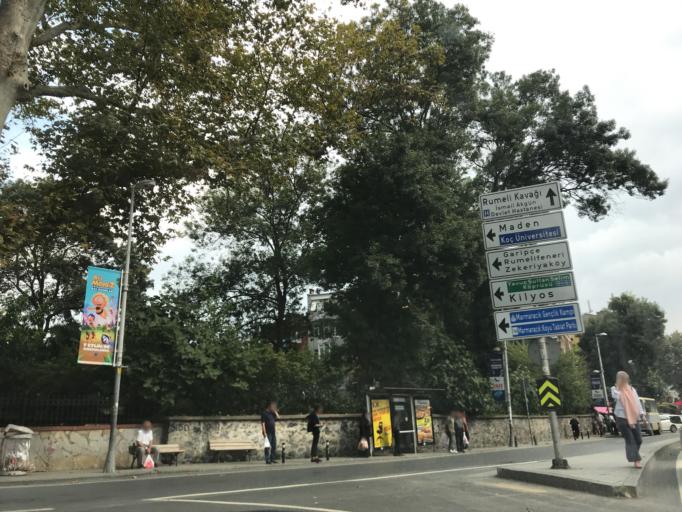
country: TR
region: Istanbul
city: Arikoey
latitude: 41.1716
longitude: 29.0534
